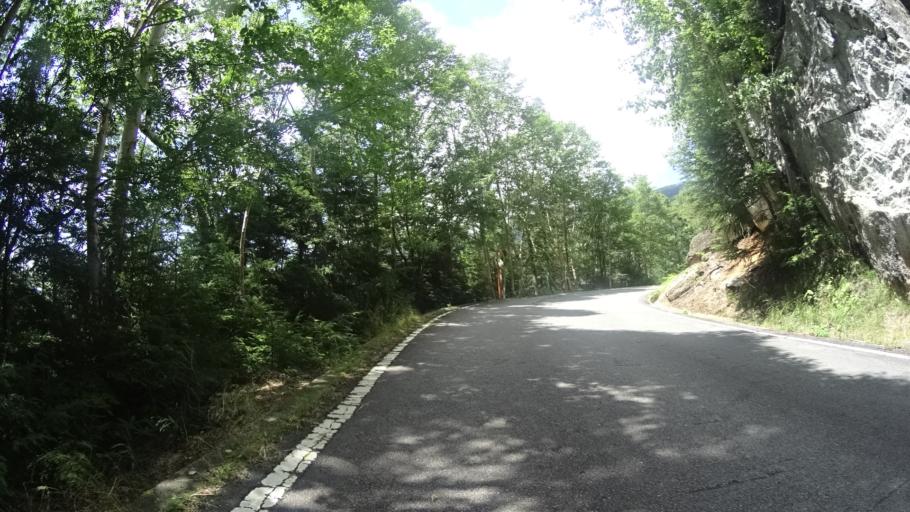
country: JP
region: Yamanashi
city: Enzan
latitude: 35.8617
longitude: 138.6573
